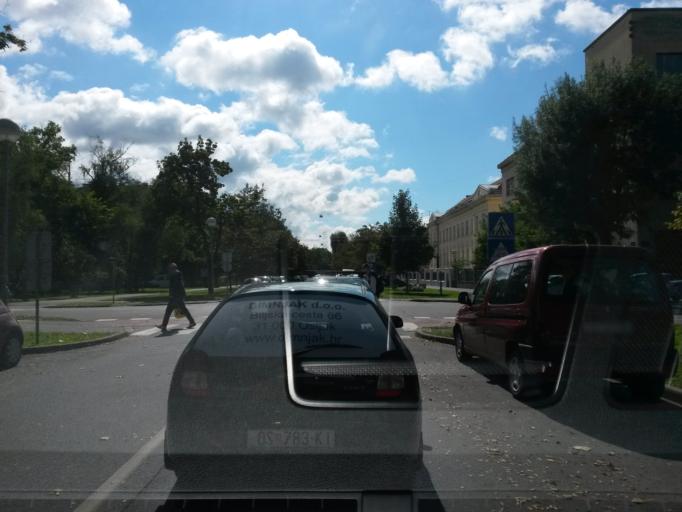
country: HR
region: Osjecko-Baranjska
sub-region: Grad Osijek
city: Osijek
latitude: 45.5586
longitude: 18.6897
